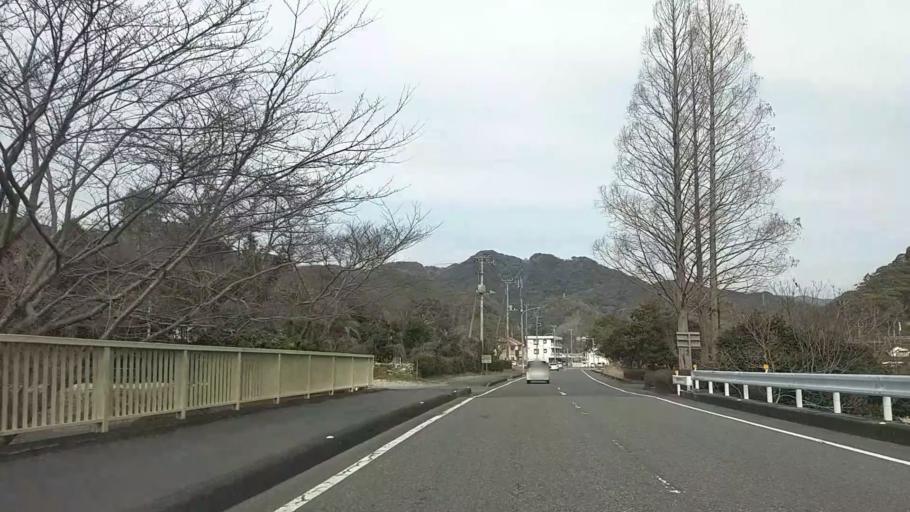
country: JP
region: Shizuoka
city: Shimoda
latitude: 34.6970
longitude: 138.9403
